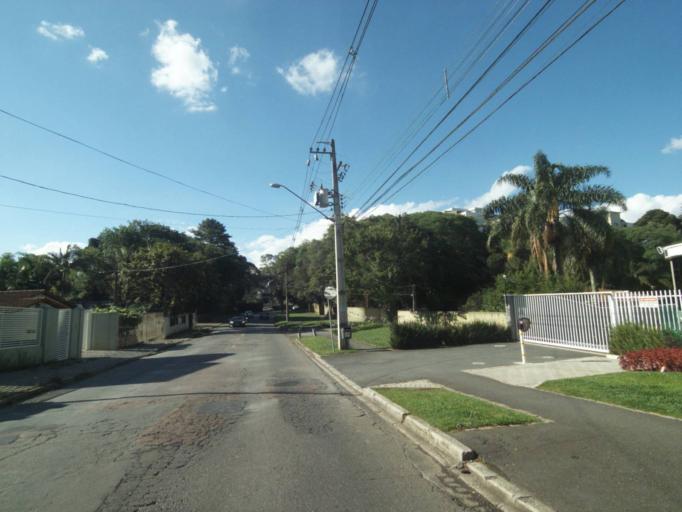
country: BR
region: Parana
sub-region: Curitiba
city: Curitiba
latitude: -25.4462
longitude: -49.3211
